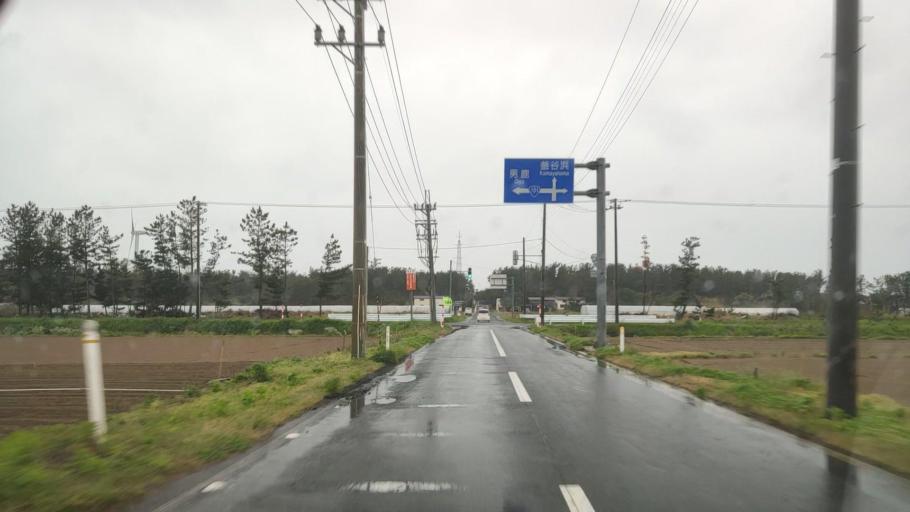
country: JP
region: Akita
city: Noshiromachi
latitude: 40.0976
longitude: 139.9678
